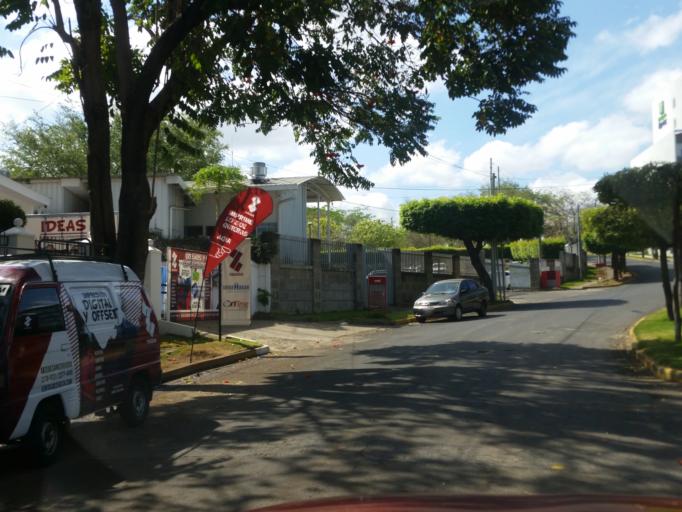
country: NI
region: Managua
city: Managua
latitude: 12.1048
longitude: -86.2556
